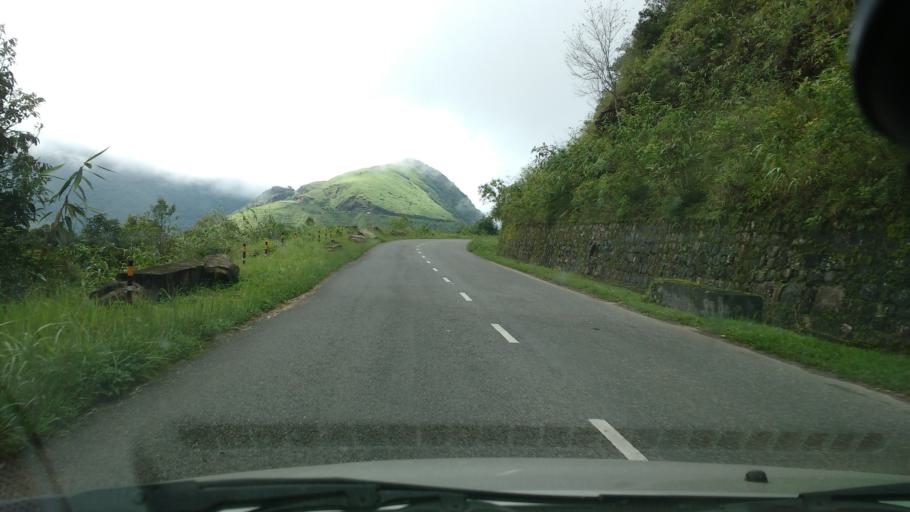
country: IN
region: Meghalaya
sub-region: East Khasi Hills
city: Shillong
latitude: 25.3797
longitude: 91.8736
